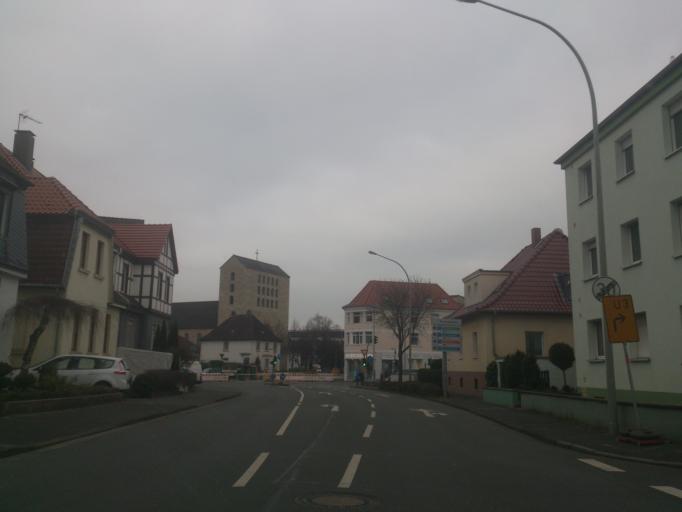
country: DE
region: North Rhine-Westphalia
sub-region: Regierungsbezirk Detmold
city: Paderborn
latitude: 51.7244
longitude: 8.7612
